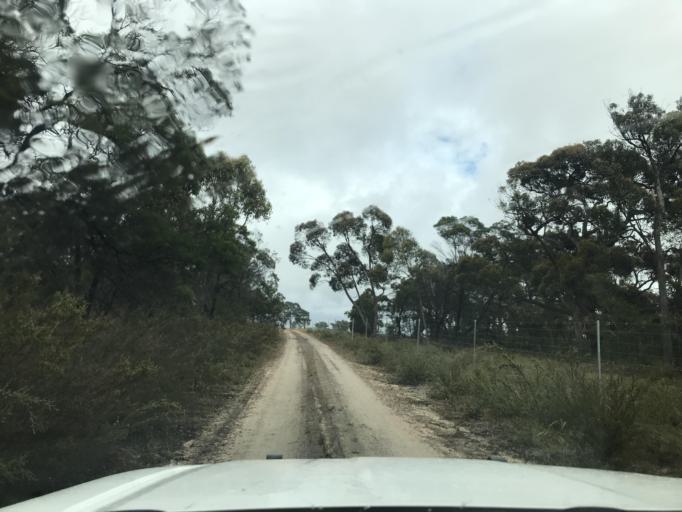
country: AU
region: South Australia
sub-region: Wattle Range
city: Penola
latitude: -37.2637
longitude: 141.3041
